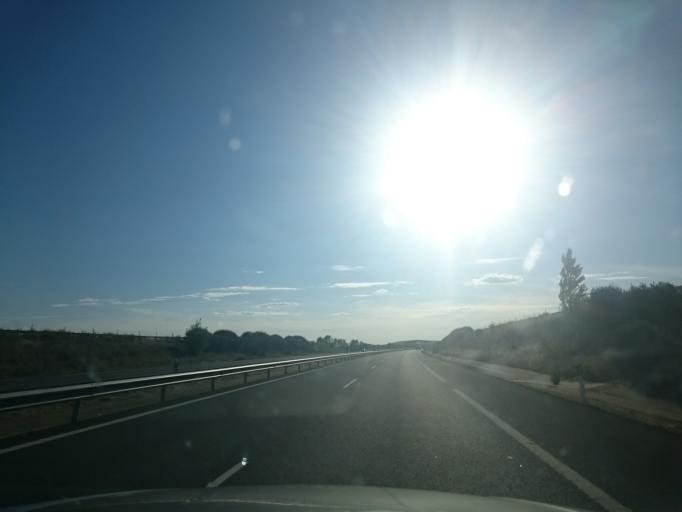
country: ES
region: Castille and Leon
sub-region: Provincia de Burgos
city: Villasandino
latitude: 42.3934
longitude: -4.0959
